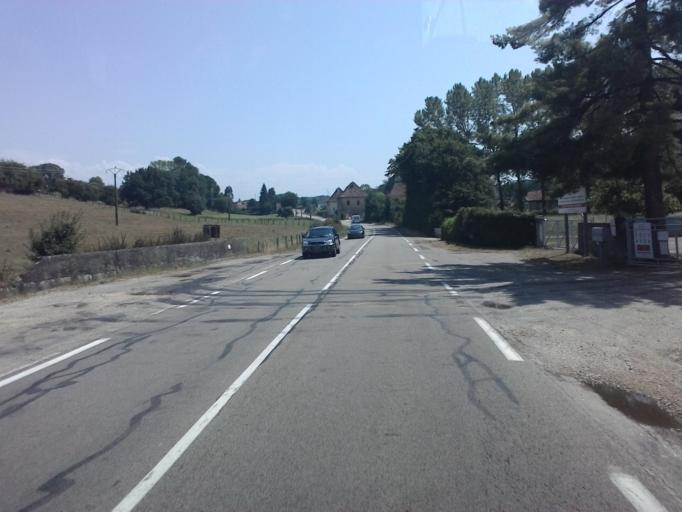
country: FR
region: Rhone-Alpes
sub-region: Departement de l'Isere
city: La Batie-Montgascon
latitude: 45.5878
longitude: 5.5405
